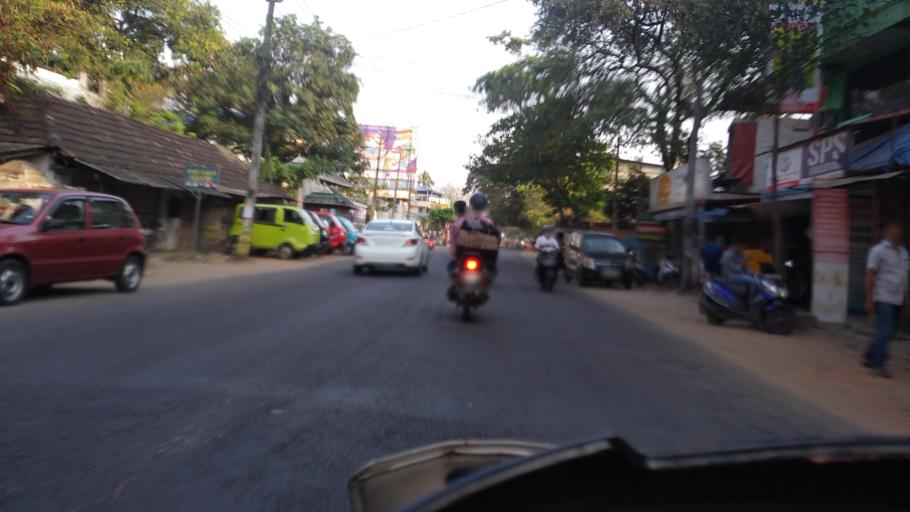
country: IN
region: Kerala
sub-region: Thrissur District
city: Thanniyam
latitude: 10.3973
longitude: 76.1151
